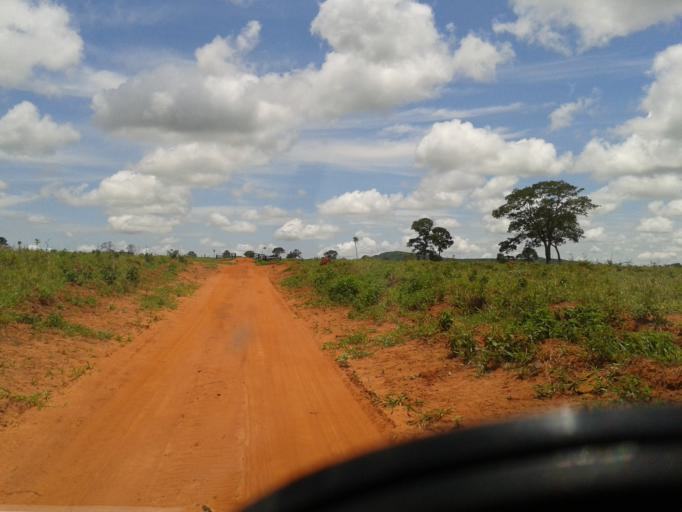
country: BR
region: Minas Gerais
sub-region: Santa Vitoria
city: Santa Vitoria
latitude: -19.0098
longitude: -49.9249
